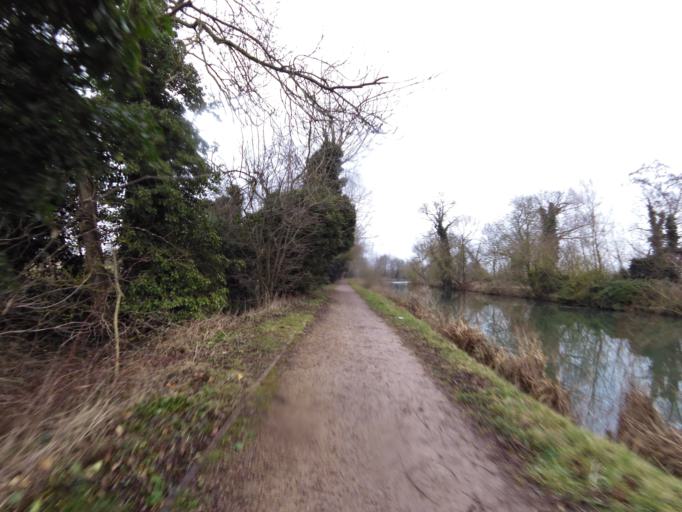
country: GB
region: England
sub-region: Cambridgeshire
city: Waterbeach
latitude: 52.2539
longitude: 0.1905
